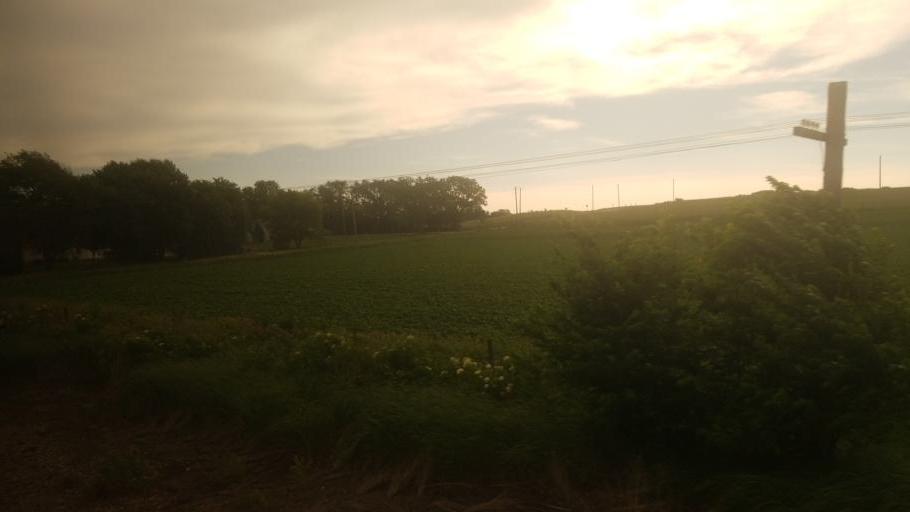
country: US
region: Kansas
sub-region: Osage County
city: Carbondale
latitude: 38.9127
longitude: -95.6987
